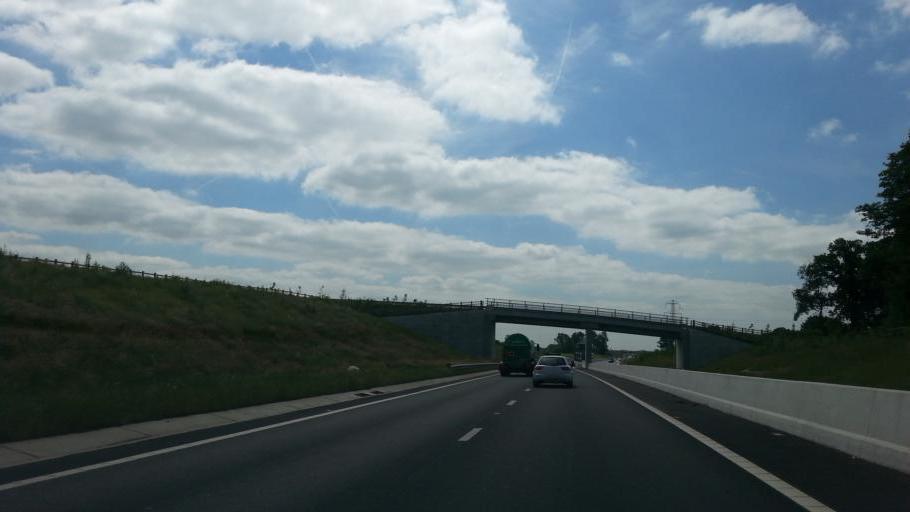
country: GB
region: England
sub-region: Cheshire East
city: Mere
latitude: 53.3268
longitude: -2.4221
